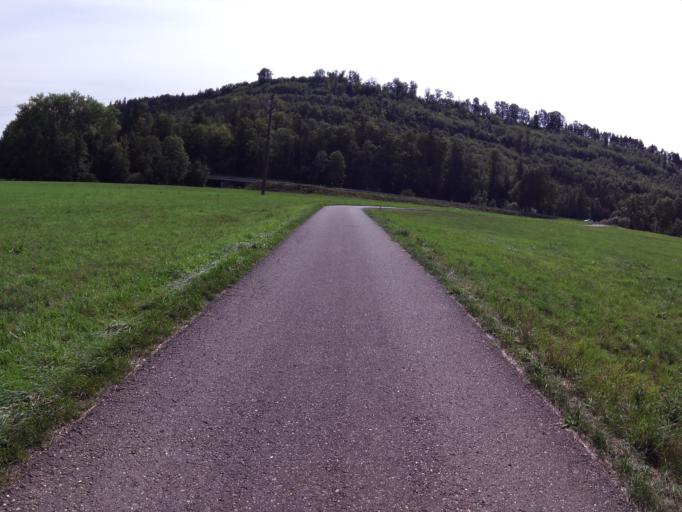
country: DE
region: Baden-Wuerttemberg
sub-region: Freiburg Region
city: Sulz am Neckar
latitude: 48.3967
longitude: 8.6434
